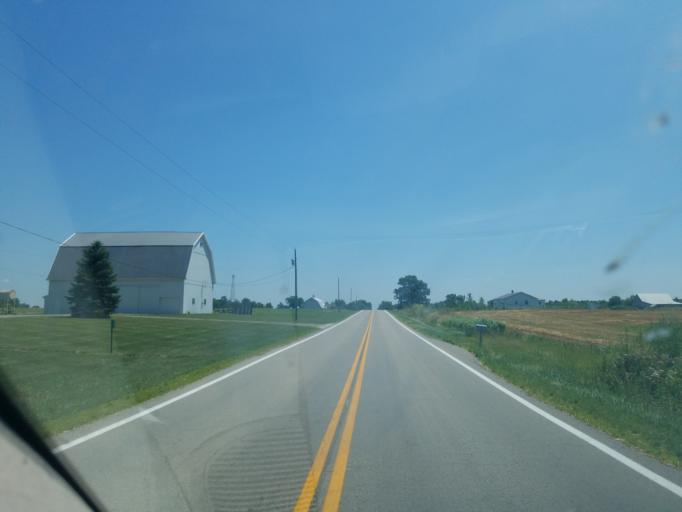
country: US
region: Ohio
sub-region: Mercer County
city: Rockford
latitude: 40.7425
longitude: -84.7154
